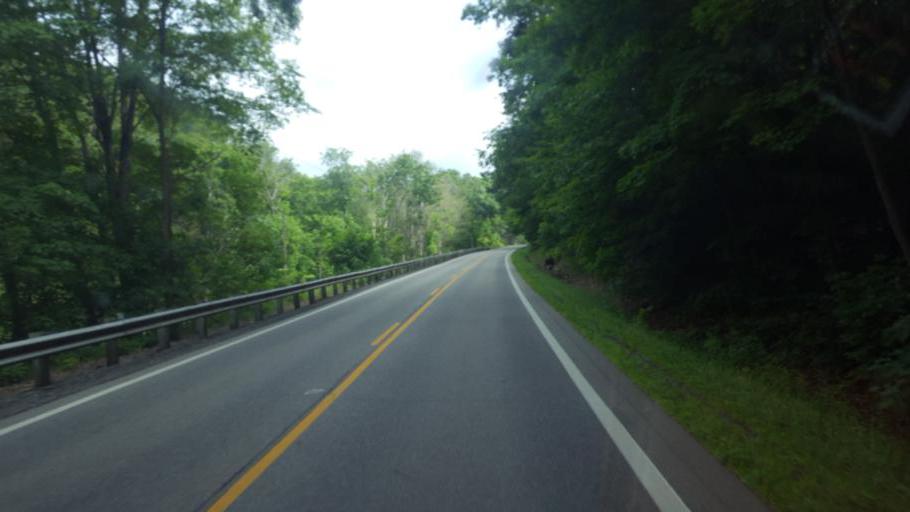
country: US
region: Ohio
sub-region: Columbiana County
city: Salineville
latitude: 40.6561
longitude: -80.8096
